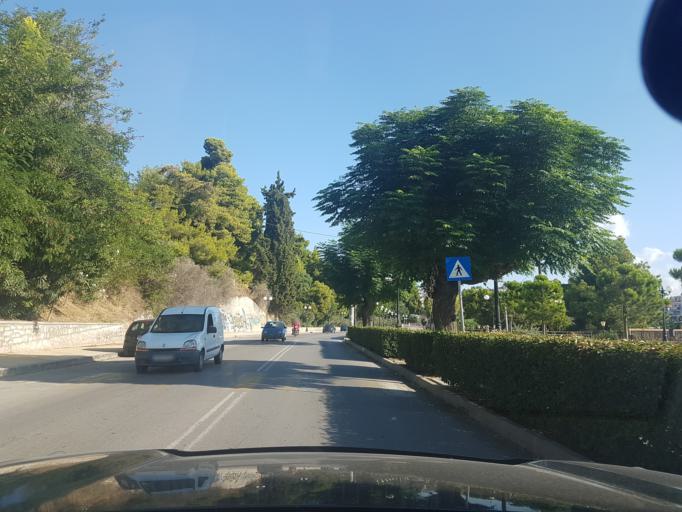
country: GR
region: Central Greece
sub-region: Nomos Evvoias
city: Chalkida
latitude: 38.4652
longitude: 23.5880
